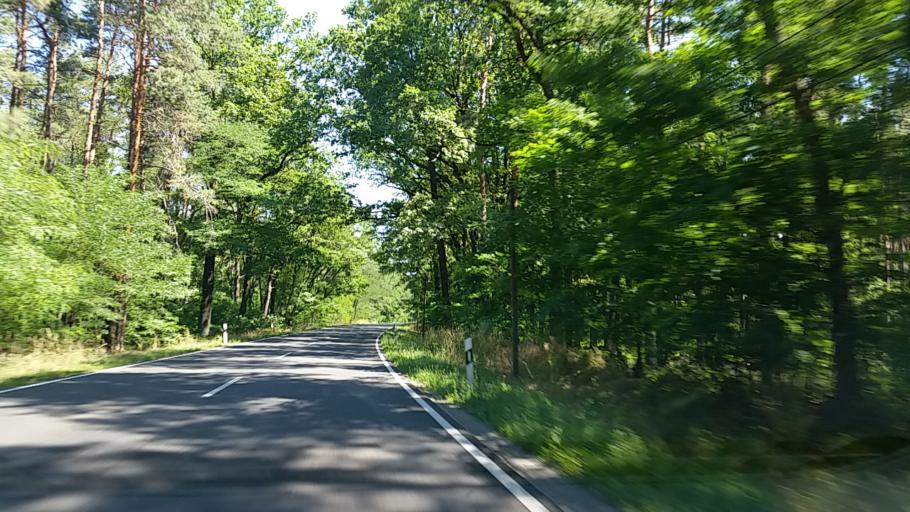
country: DE
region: Saxony-Anhalt
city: Kemberg
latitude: 51.7381
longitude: 12.6216
